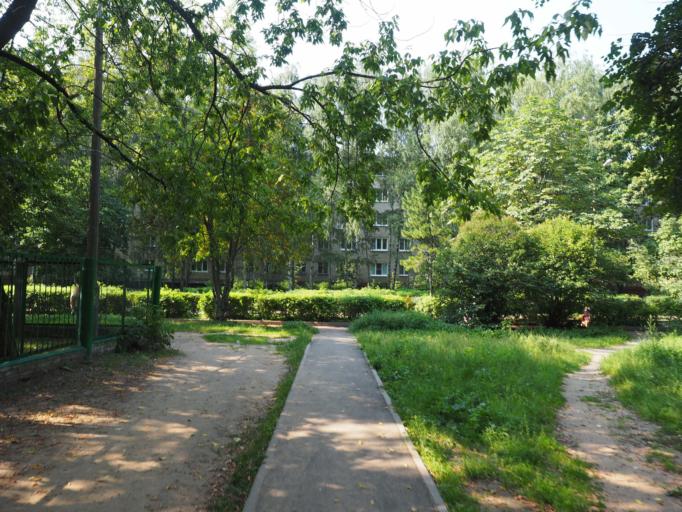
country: RU
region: Moskovskaya
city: Udel'naya
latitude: 55.6245
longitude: 38.0042
